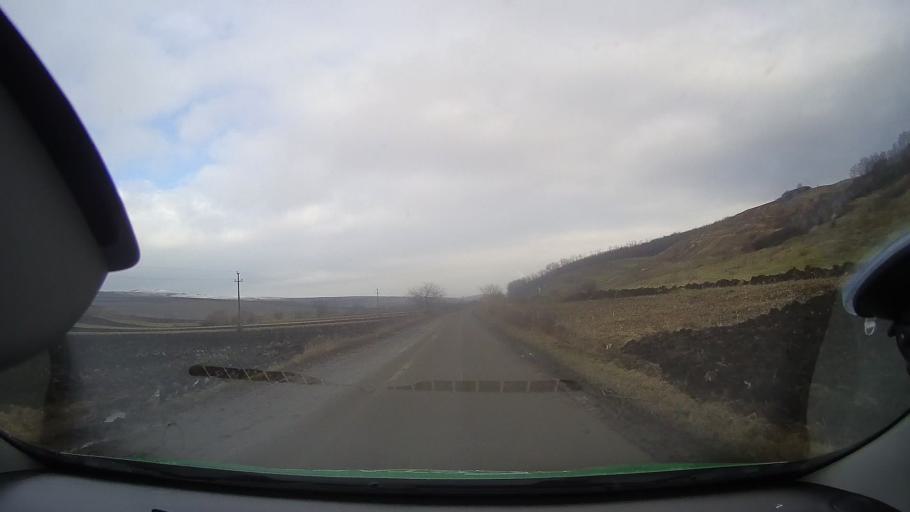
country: RO
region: Mures
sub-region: Comuna Ludus
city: Gheja
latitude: 46.4027
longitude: 24.0596
